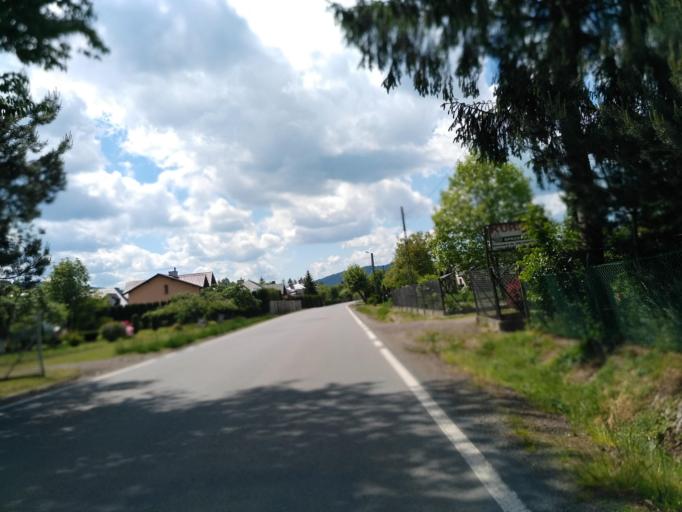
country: PL
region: Subcarpathian Voivodeship
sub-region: Powiat krosnienski
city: Dukla
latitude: 49.5757
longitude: 21.6966
